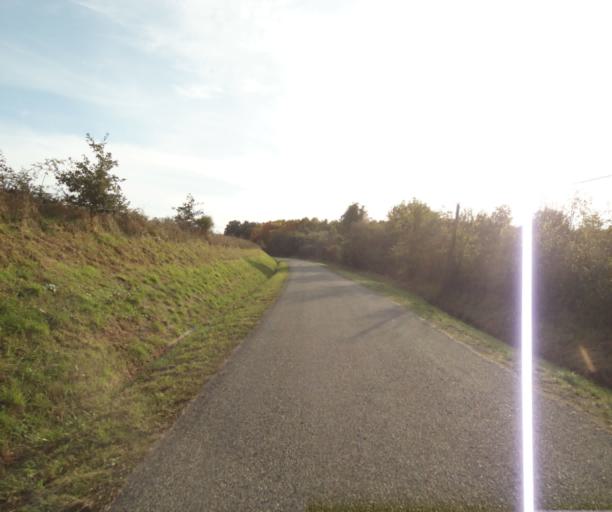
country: FR
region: Midi-Pyrenees
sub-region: Departement du Tarn-et-Garonne
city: Campsas
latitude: 43.8809
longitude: 1.3214
